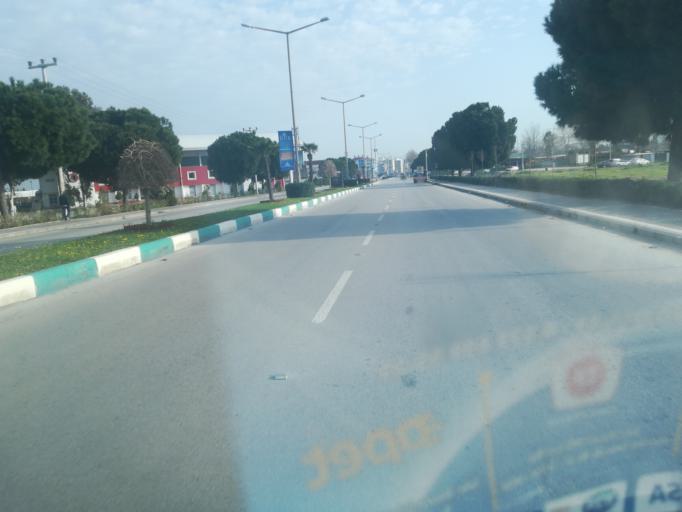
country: TR
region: Osmaniye
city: Osmaniye
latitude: 37.0517
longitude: 36.2299
